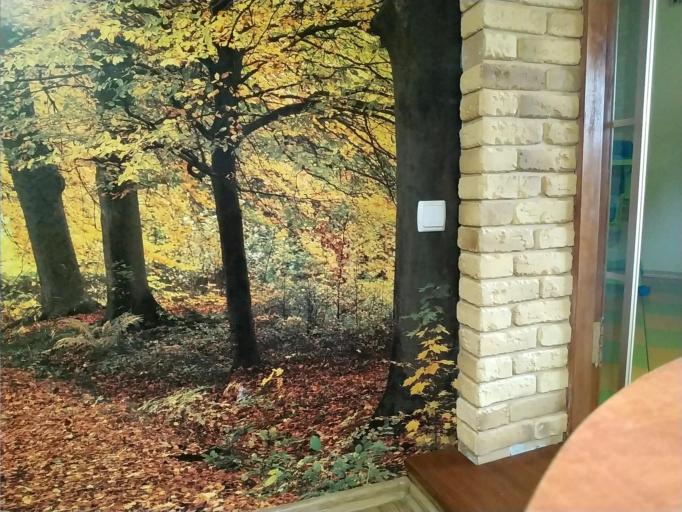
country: RU
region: Smolensk
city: Dorogobuzh
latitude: 54.9449
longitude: 33.2992
